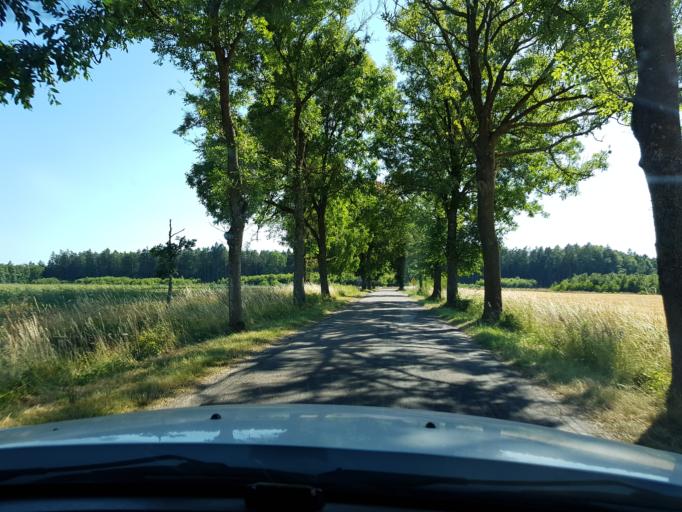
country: PL
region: West Pomeranian Voivodeship
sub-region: Powiat swidwinski
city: Slawoborze
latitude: 53.8383
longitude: 15.7122
